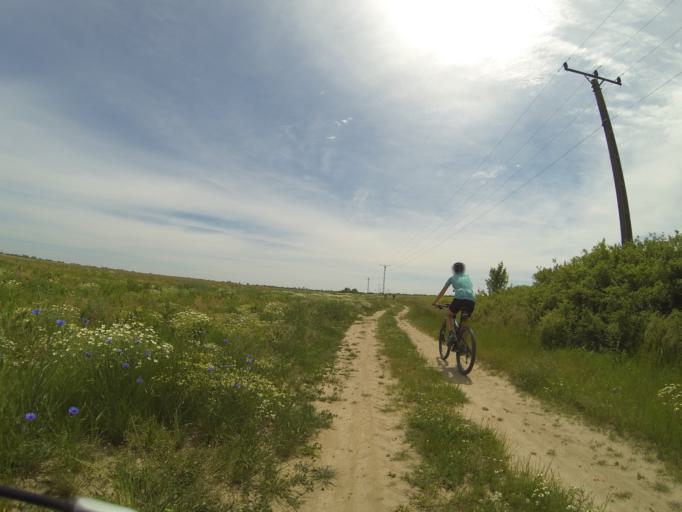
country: RO
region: Dolj
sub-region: Comuna Ghindeni
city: Ghindeni
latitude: 44.2052
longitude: 23.9614
